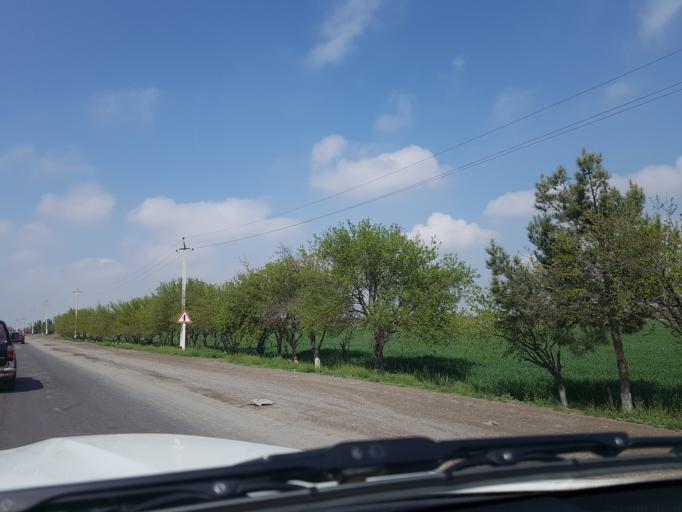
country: TM
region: Lebap
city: Turkmenabat
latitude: 38.9676
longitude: 63.6562
